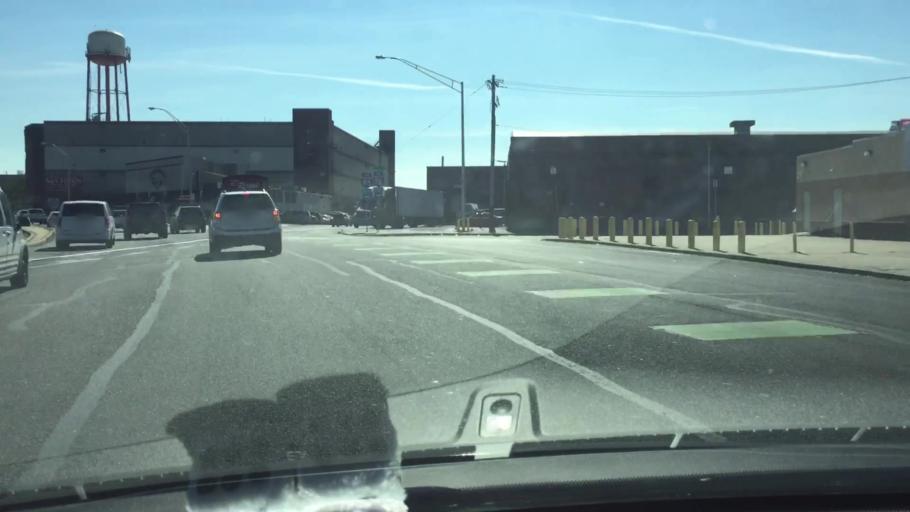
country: US
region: New Jersey
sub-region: Camden County
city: Camden
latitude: 39.9268
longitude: -75.1451
